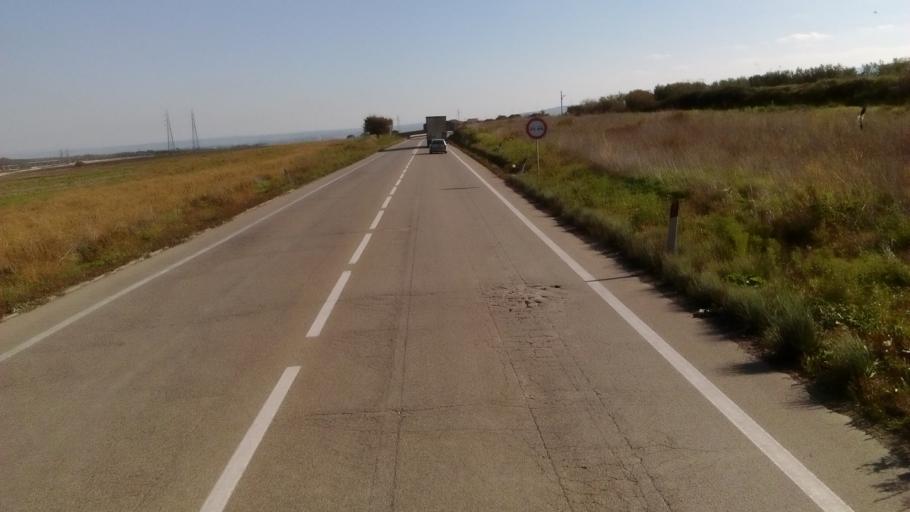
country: IT
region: Apulia
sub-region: Provincia di Foggia
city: Candela
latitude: 41.1193
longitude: 15.5743
